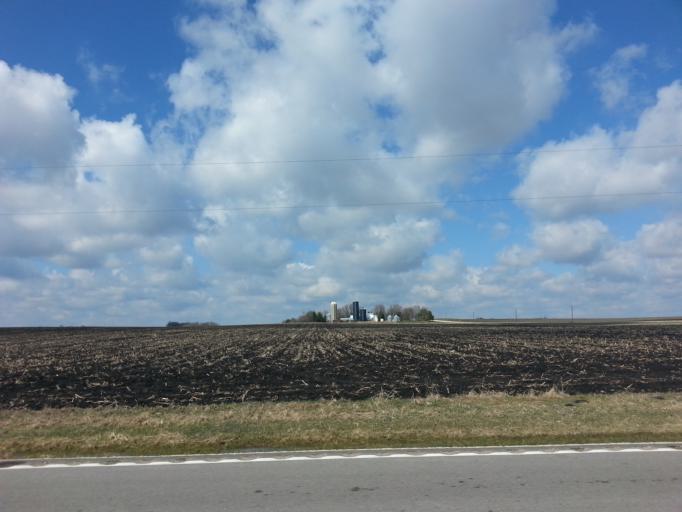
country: US
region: Minnesota
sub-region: Dodge County
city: Dodge Center
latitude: 44.0879
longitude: -92.8510
